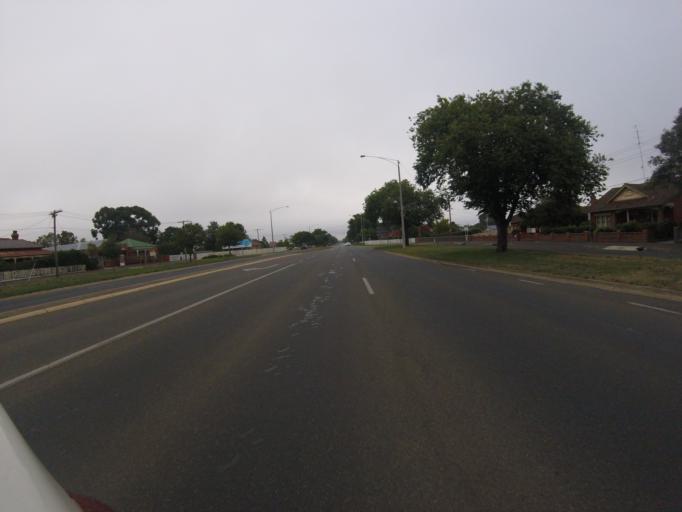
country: AU
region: Victoria
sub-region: Ballarat North
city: Canadian
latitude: -37.5592
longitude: 143.8834
